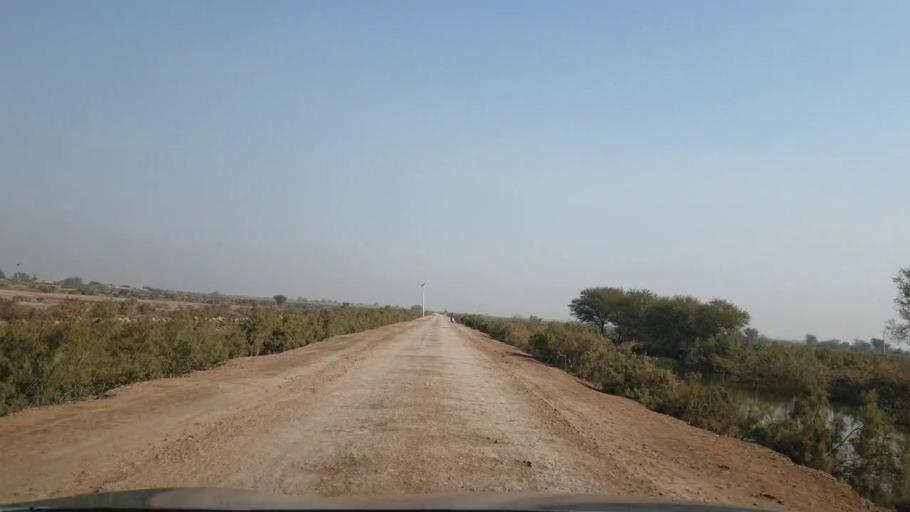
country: PK
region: Sindh
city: Berani
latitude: 25.6416
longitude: 68.8713
